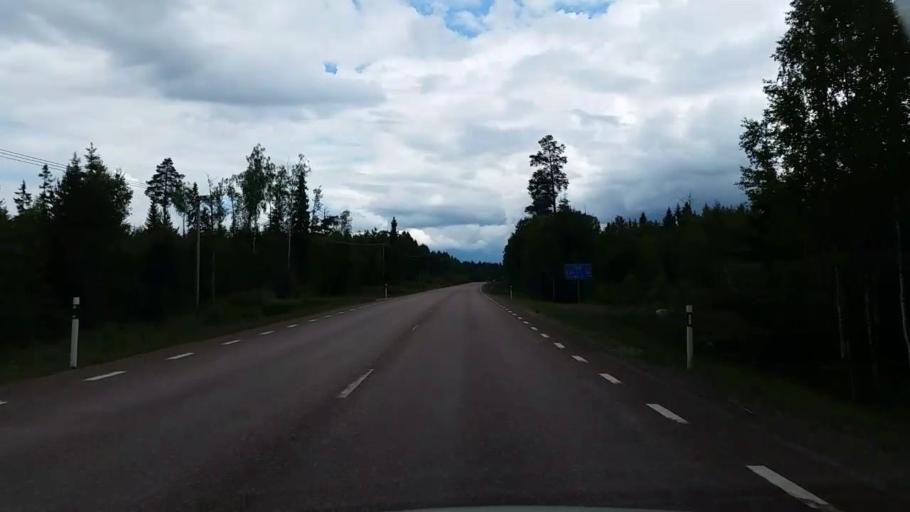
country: SE
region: Gaevleborg
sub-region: Hofors Kommun
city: Hofors
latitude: 60.5023
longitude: 16.4325
